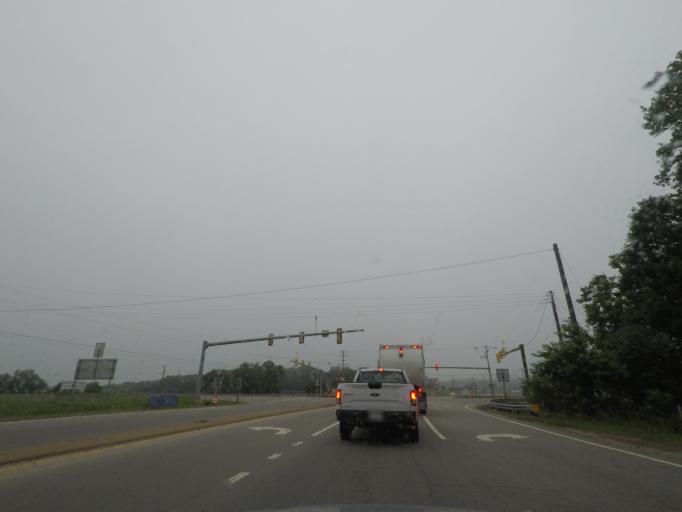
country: US
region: Virginia
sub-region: Buckingham County
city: Buckingham
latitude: 37.5285
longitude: -78.4923
